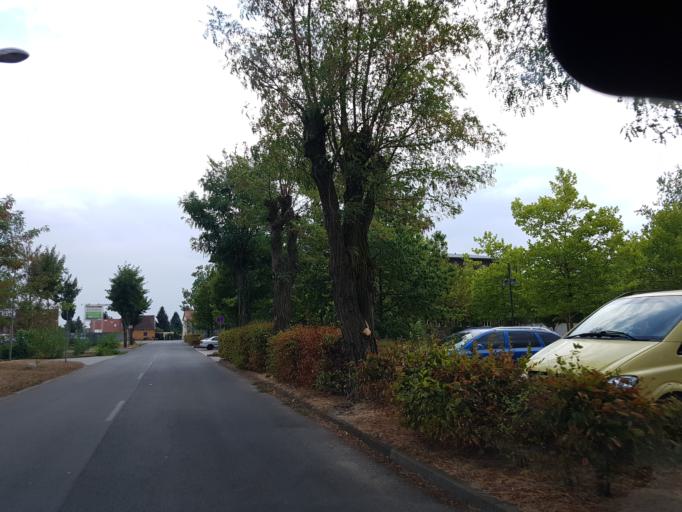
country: DE
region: Saxony-Anhalt
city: Abtsdorf
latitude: 51.8654
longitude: 12.6864
